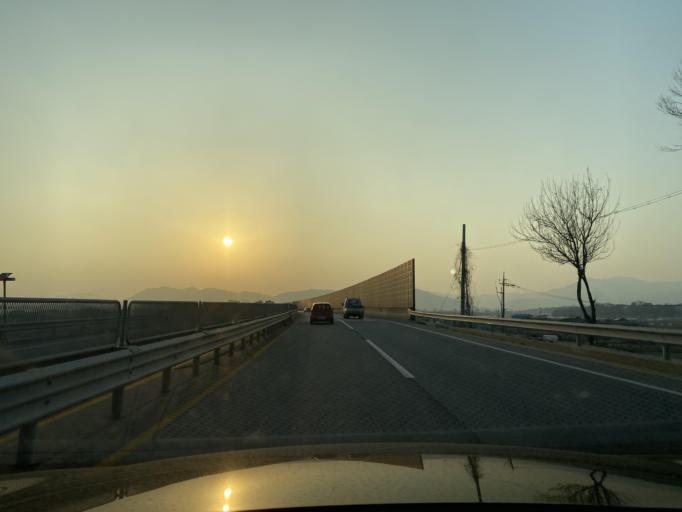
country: KR
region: Chungcheongnam-do
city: Hongsung
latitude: 36.6920
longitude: 126.7247
